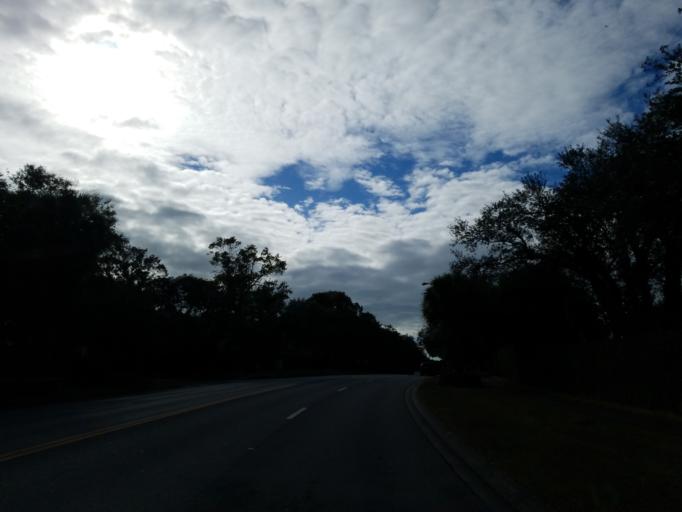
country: US
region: Florida
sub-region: Hillsborough County
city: Bloomingdale
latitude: 27.8825
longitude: -82.2414
